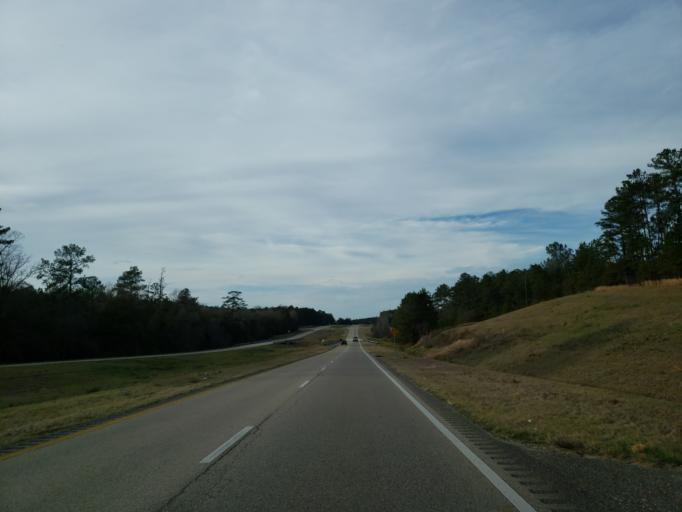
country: US
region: Mississippi
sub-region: Wayne County
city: Waynesboro
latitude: 31.6226
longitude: -88.5830
